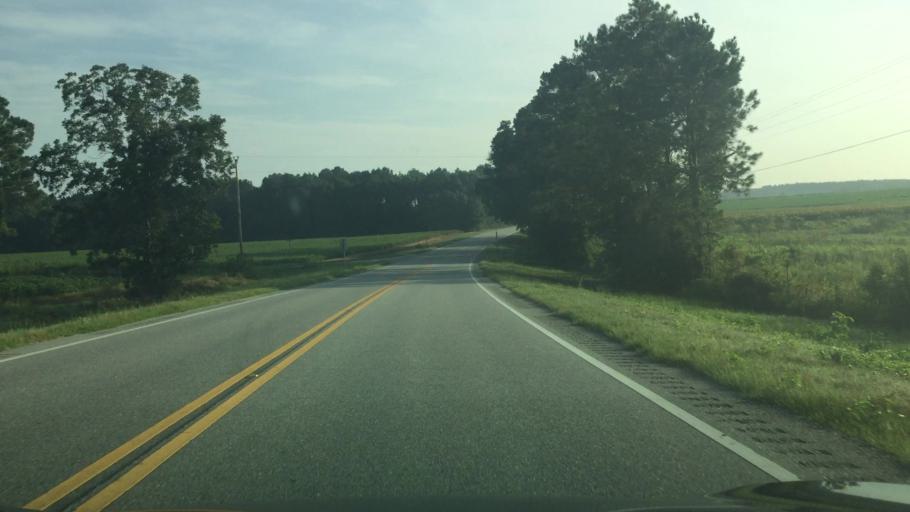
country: US
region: Alabama
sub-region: Covington County
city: Andalusia
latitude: 31.1711
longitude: -86.4599
